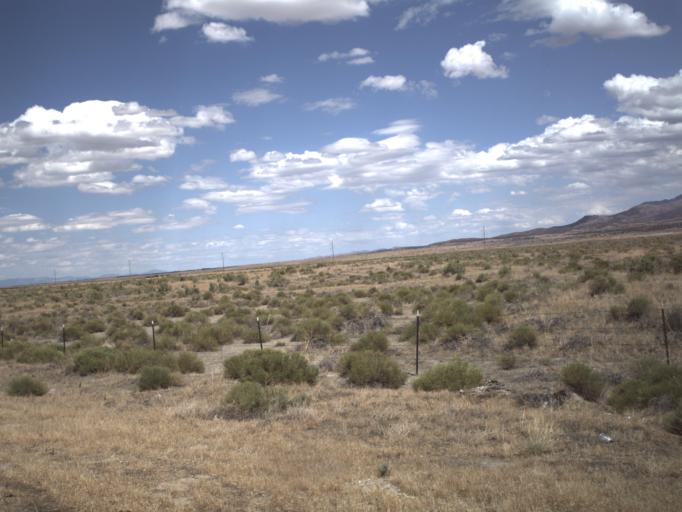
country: US
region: Utah
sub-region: Millard County
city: Delta
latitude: 39.2354
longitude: -112.4299
